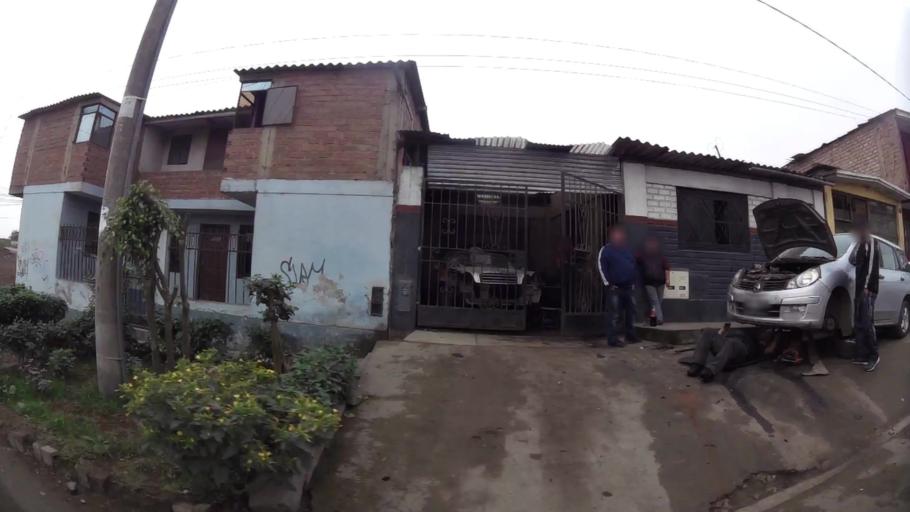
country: PE
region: Lima
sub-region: Lima
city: Surco
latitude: -12.1885
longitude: -76.9299
